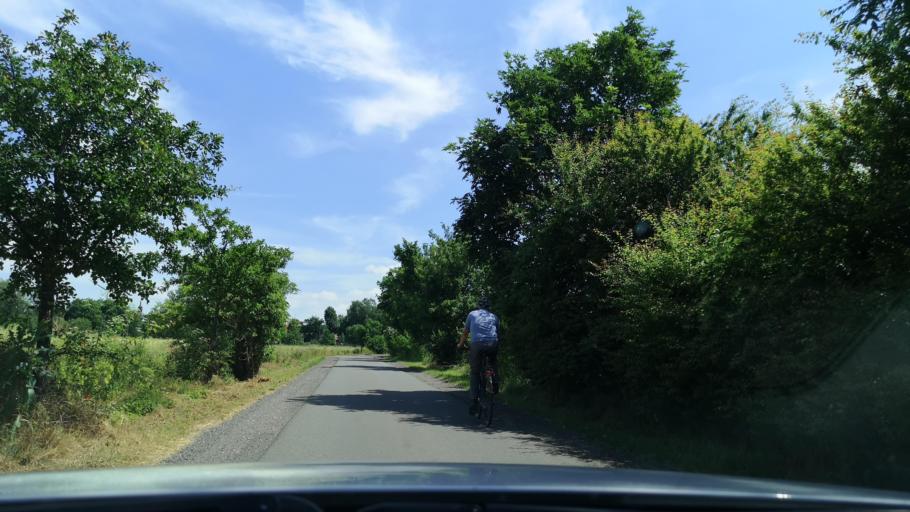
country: DE
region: Thuringia
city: Eberstedt
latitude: 51.0458
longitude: 11.5926
